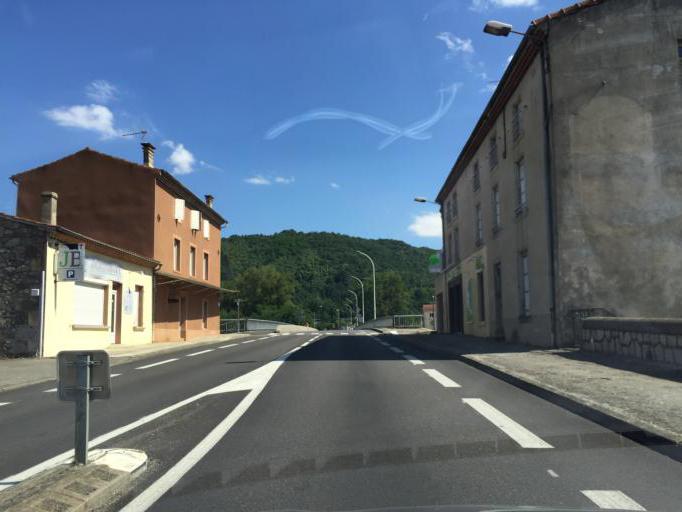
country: FR
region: Rhone-Alpes
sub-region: Departement de l'Ardeche
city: Saint-Jean-de-Muzols
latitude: 45.0756
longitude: 4.8162
